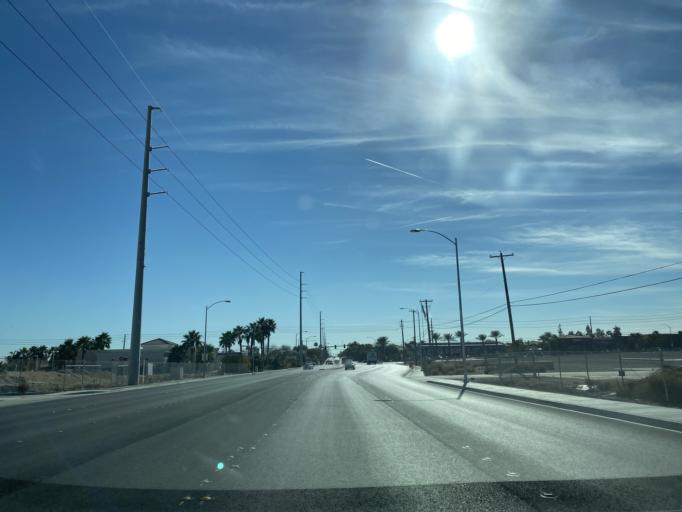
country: US
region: Nevada
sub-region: Clark County
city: North Las Vegas
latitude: 36.2414
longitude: -115.1437
